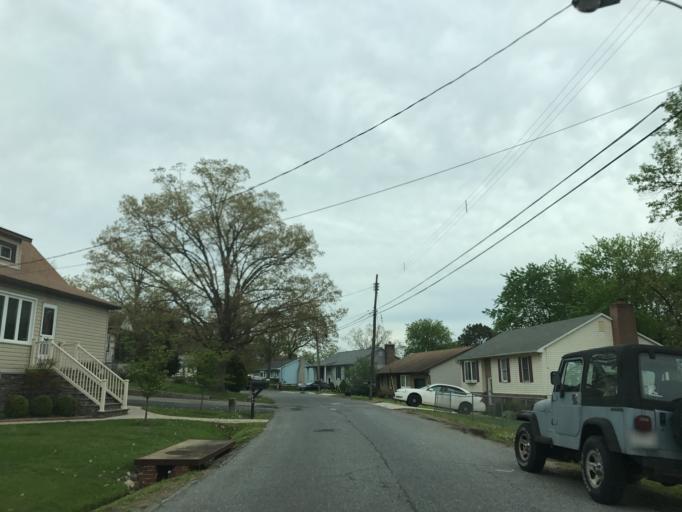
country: US
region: Maryland
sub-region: Baltimore County
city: Rosedale
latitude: 39.3094
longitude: -76.5125
